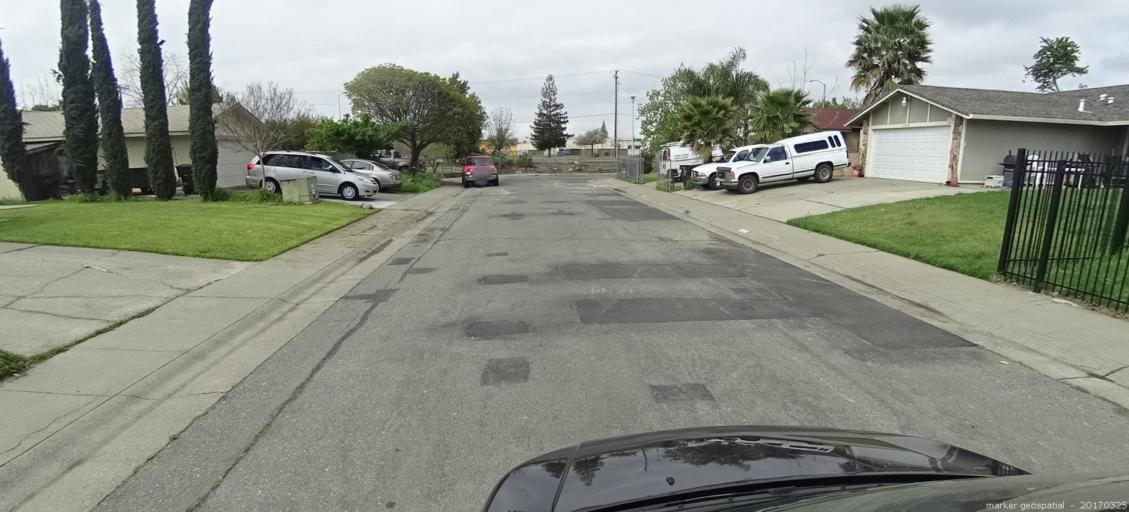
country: US
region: California
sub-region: Sacramento County
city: Florin
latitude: 38.5167
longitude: -121.4265
